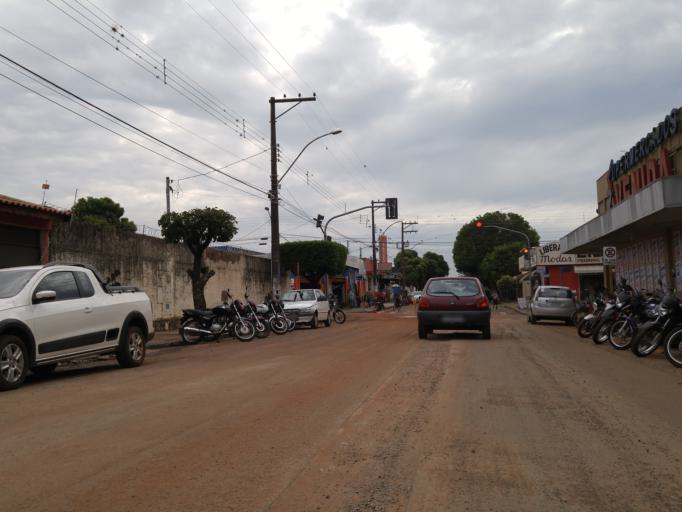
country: BR
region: Sao Paulo
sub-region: Paraguacu Paulista
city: Paraguacu Paulista
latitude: -22.4188
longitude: -50.5746
